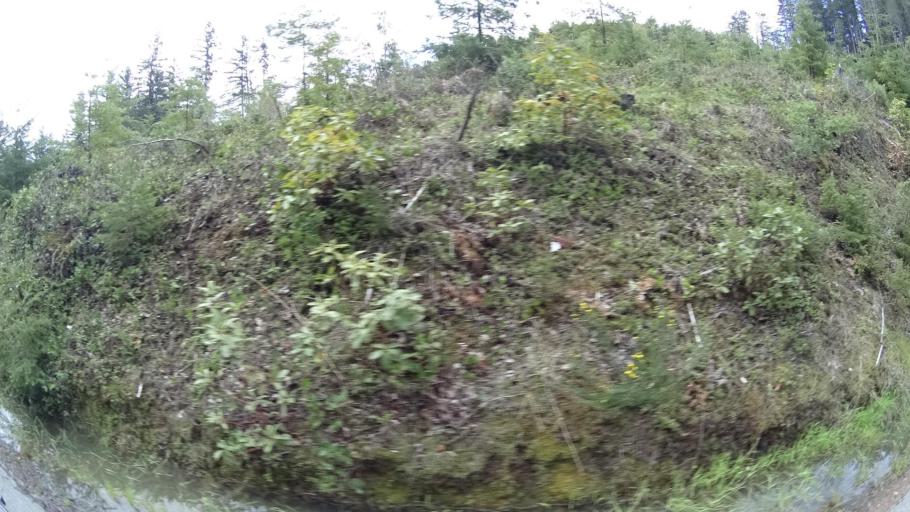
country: US
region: California
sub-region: Humboldt County
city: Blue Lake
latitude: 40.8681
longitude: -123.8977
